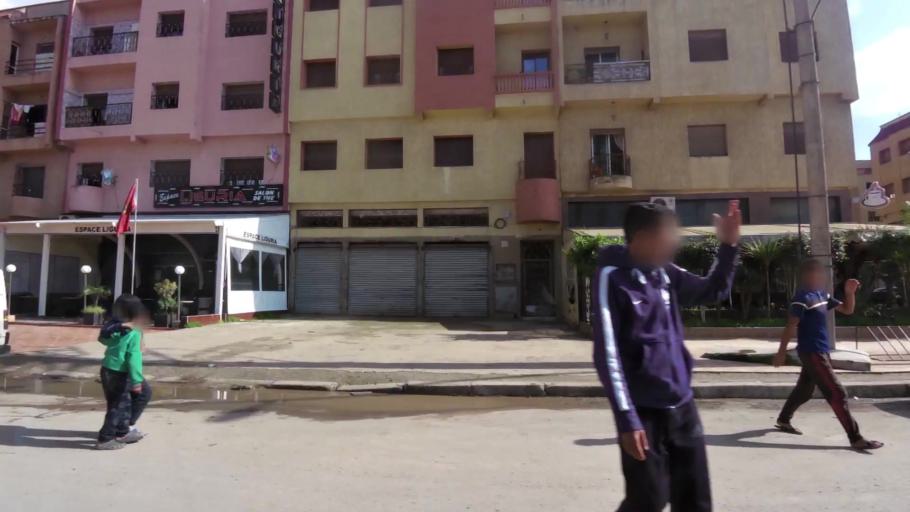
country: MA
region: Chaouia-Ouardigha
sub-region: Settat Province
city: Berrechid
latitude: 33.2684
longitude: -7.5717
